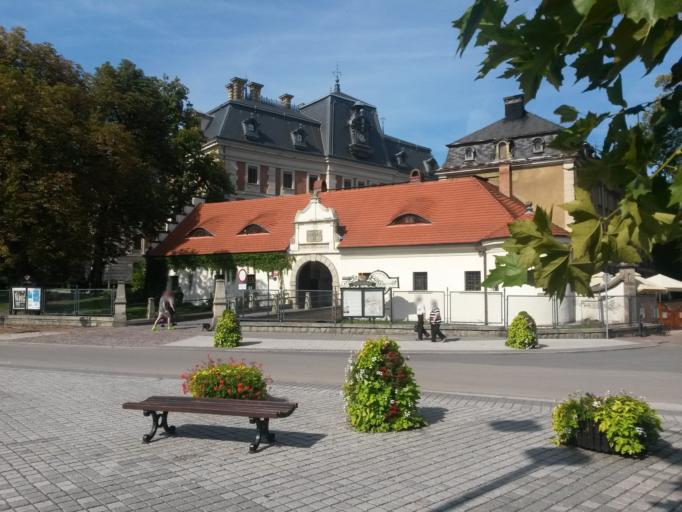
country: PL
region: Silesian Voivodeship
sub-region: Powiat pszczynski
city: Pszczyna
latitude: 49.9777
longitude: 18.9418
